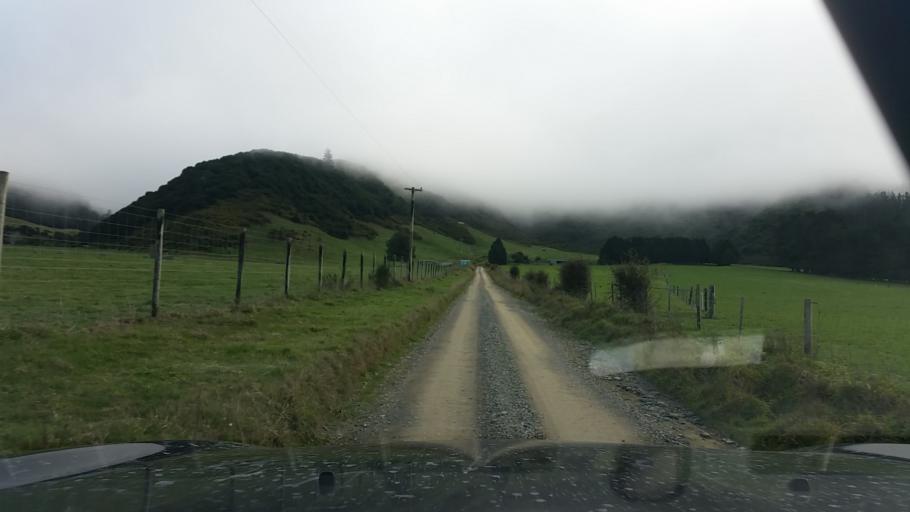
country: NZ
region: Marlborough
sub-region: Marlborough District
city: Picton
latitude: -41.1717
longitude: 173.9659
